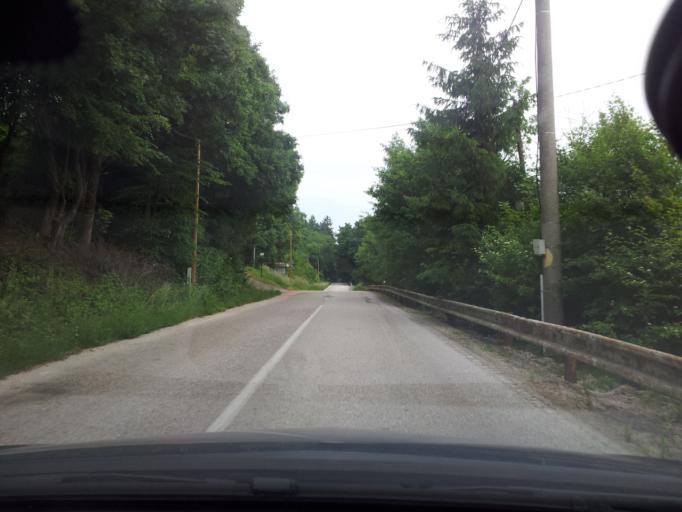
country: SK
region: Nitriansky
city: Partizanske
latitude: 48.5824
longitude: 18.4531
